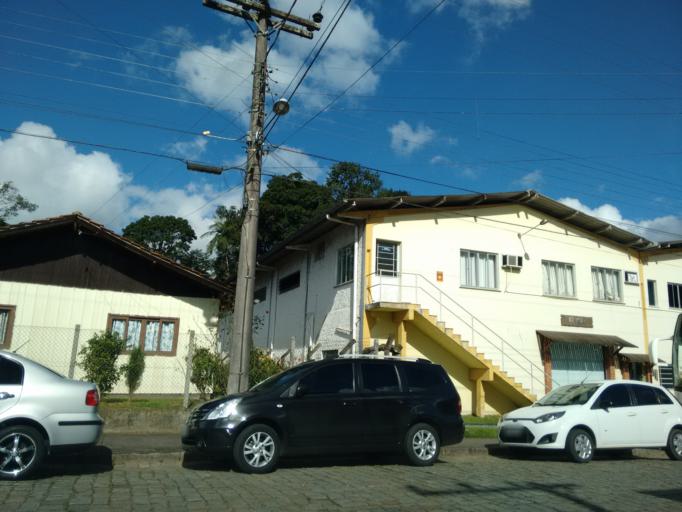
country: BR
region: Santa Catarina
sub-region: Pomerode
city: Pomerode
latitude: -26.7507
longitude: -49.1786
